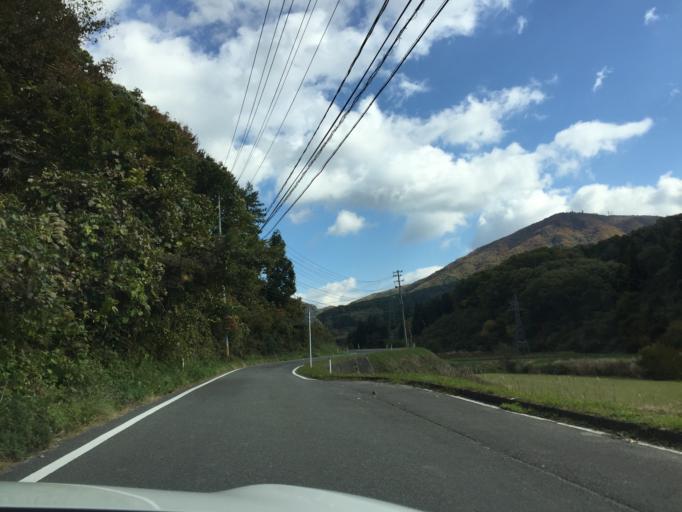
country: JP
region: Fukushima
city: Funehikimachi-funehiki
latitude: 37.2927
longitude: 140.6628
